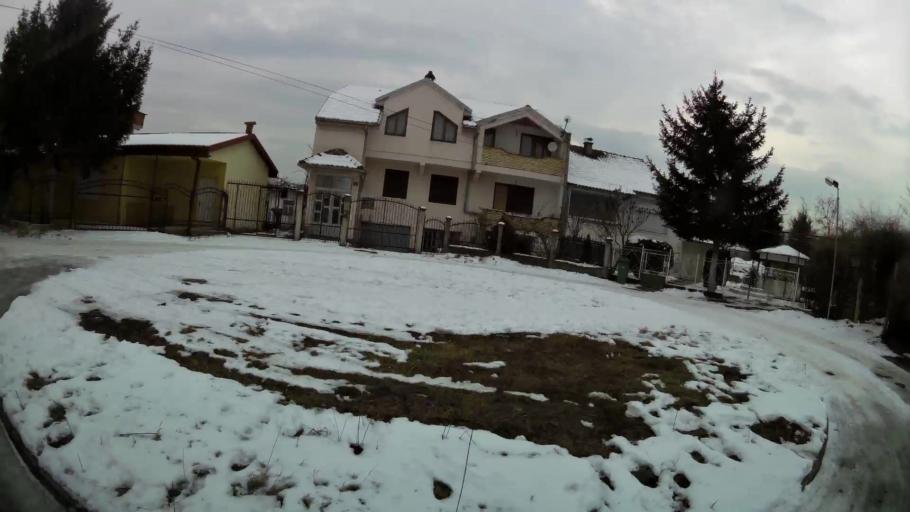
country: MK
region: Butel
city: Butel
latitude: 42.0345
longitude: 21.4421
